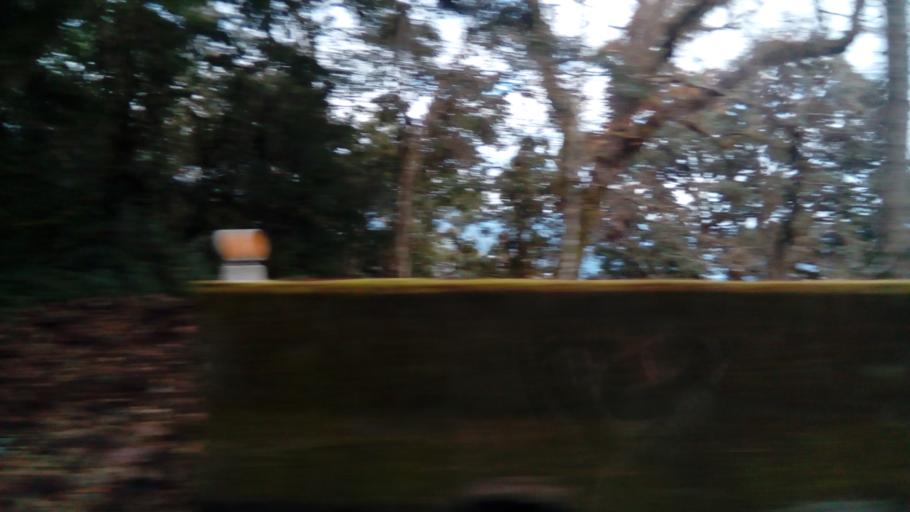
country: TW
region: Taiwan
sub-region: Hualien
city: Hualian
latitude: 24.3996
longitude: 121.3647
